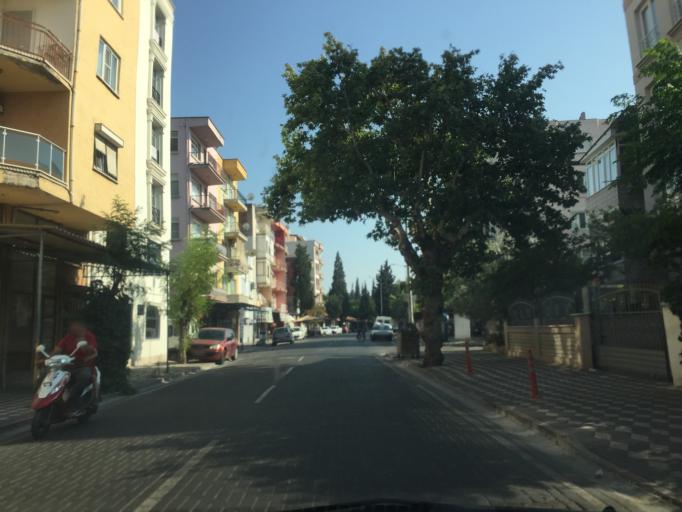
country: TR
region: Manisa
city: Akhisar
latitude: 38.9150
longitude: 27.8420
